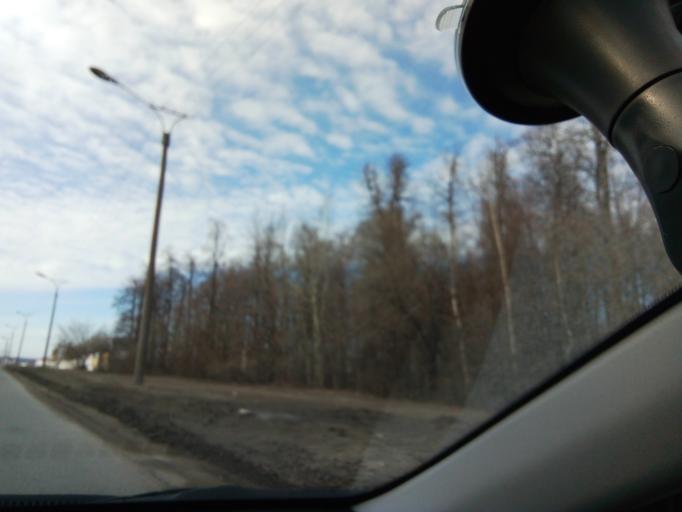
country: RU
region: Chuvashia
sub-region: Cheboksarskiy Rayon
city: Cheboksary
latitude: 56.0980
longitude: 47.2572
